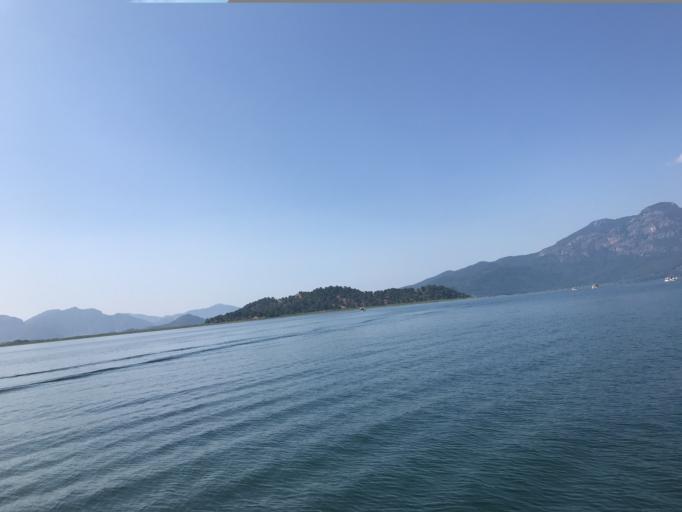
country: TR
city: Dalyan
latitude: 36.9106
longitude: 28.6530
